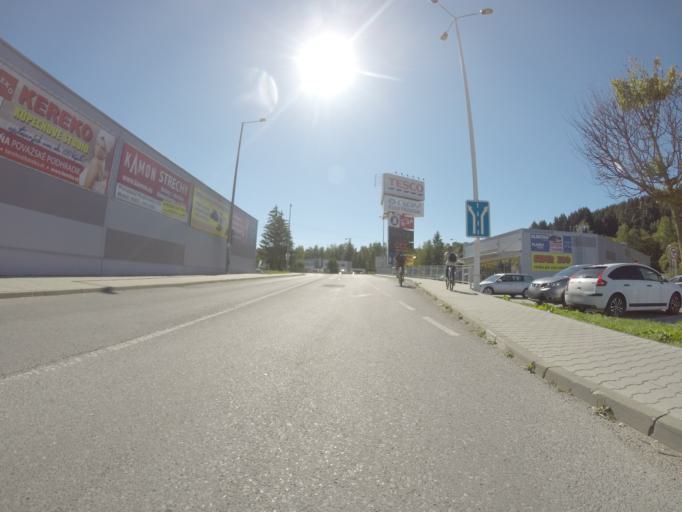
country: SK
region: Trenciansky
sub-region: Okres Povazska Bystrica
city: Povazska Bystrica
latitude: 49.1021
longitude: 18.4613
